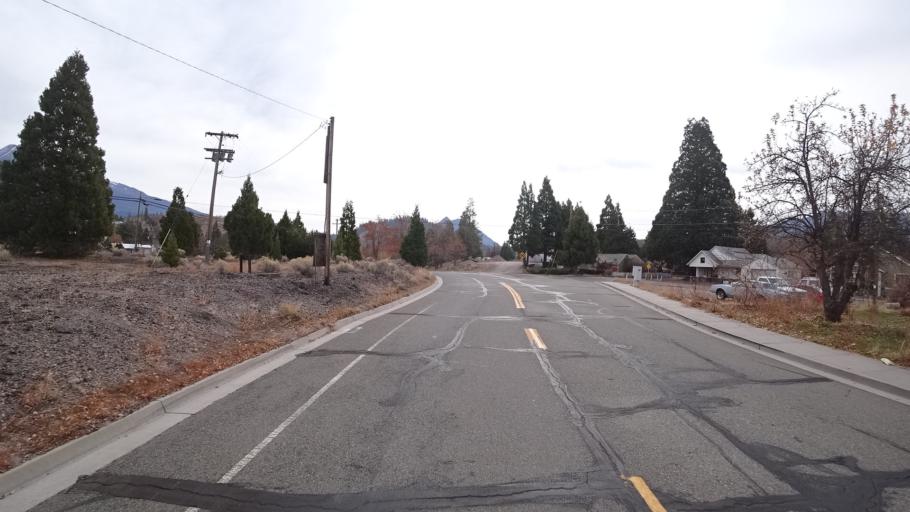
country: US
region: California
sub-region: Siskiyou County
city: Weed
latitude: 41.4288
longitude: -122.3877
